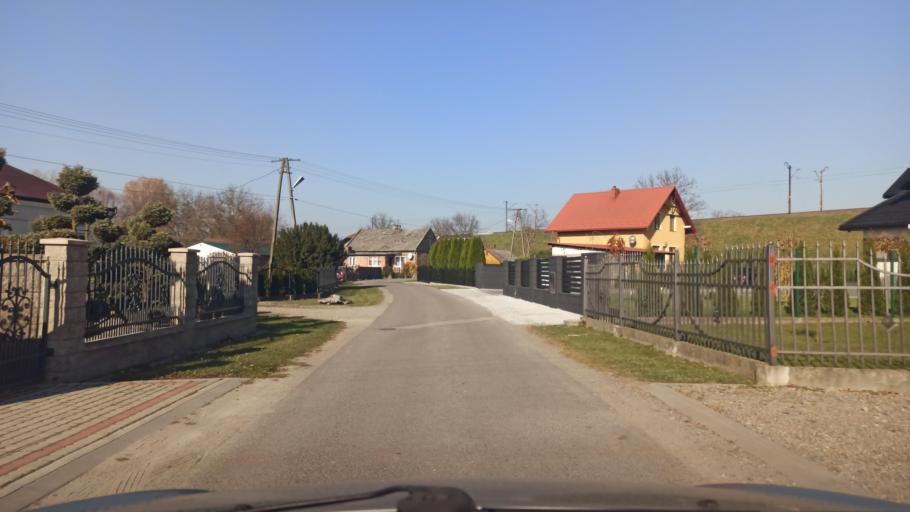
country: PL
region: Subcarpathian Voivodeship
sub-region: Powiat jaroslawski
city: Radymno
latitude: 49.9419
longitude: 22.8181
